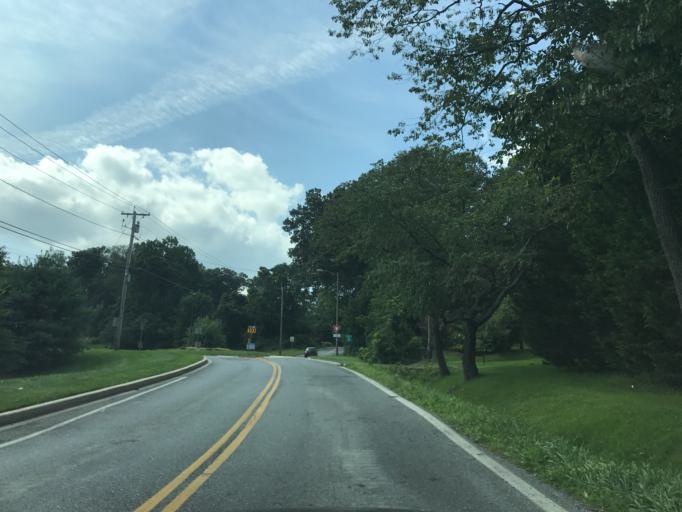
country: US
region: Maryland
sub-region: Harford County
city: South Bel Air
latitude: 39.5581
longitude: -76.3016
